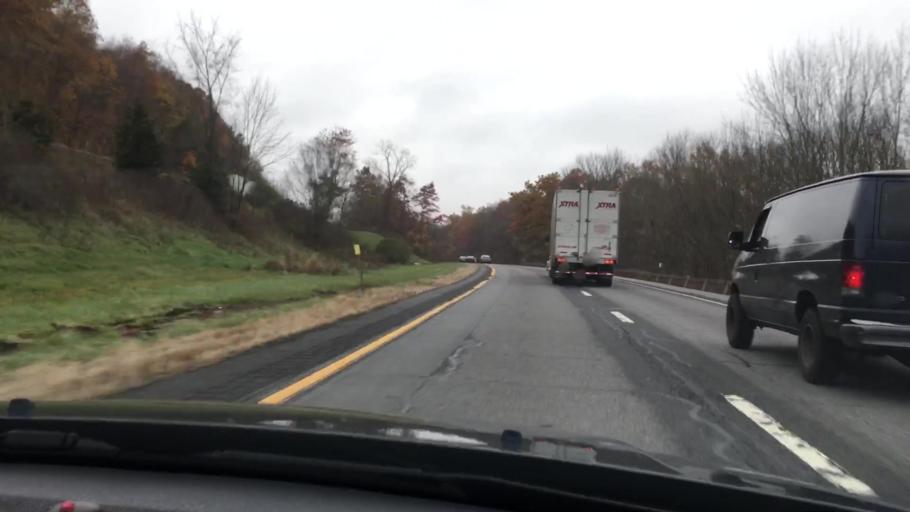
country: US
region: New York
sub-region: Putnam County
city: Lake Carmel
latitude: 41.4999
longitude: -73.6711
